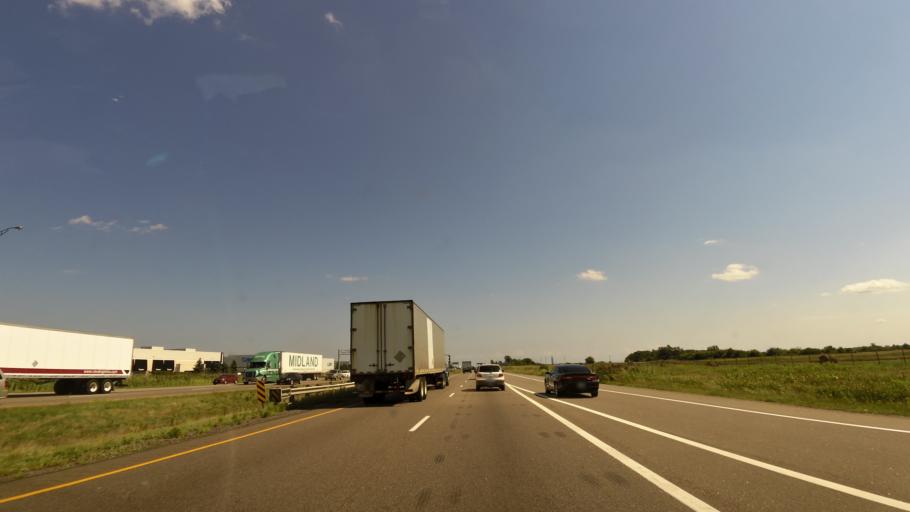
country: CA
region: Ontario
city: Oakville
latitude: 43.5097
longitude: -79.6897
